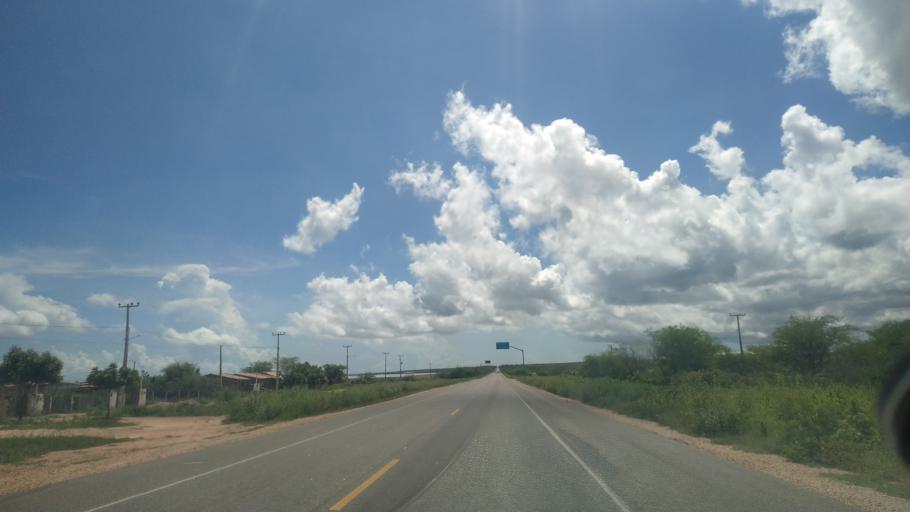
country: BR
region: Rio Grande do Norte
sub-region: Areia Branca
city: Areia Branca
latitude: -5.0560
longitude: -37.1541
